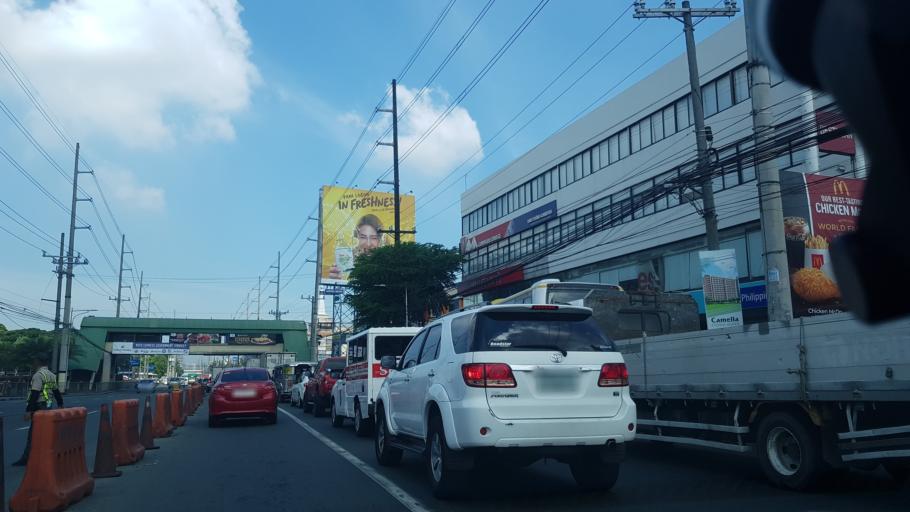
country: PH
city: Sambayanihan People's Village
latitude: 14.4343
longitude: 121.0117
